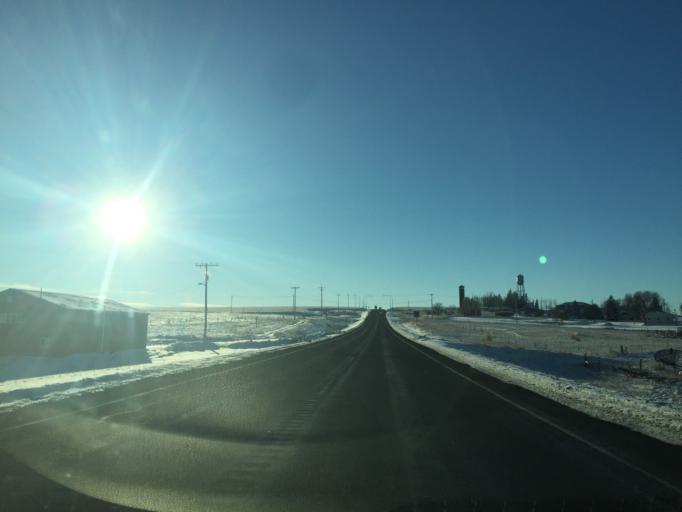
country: US
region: Washington
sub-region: Okanogan County
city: Coulee Dam
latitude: 47.7079
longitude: -118.9335
